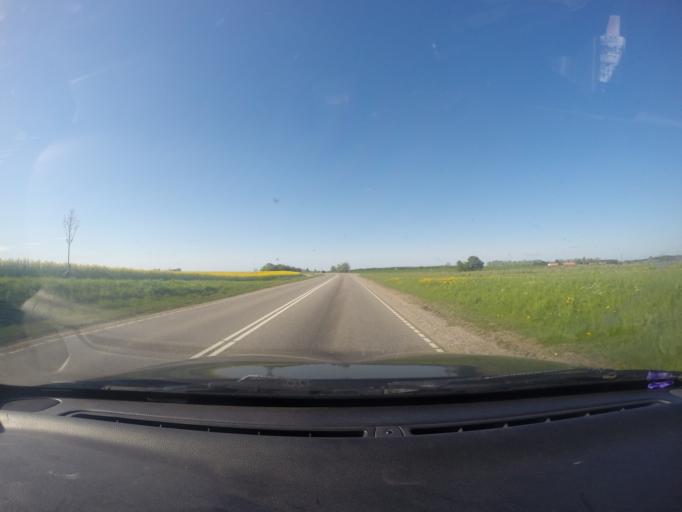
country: DK
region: Capital Region
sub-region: Hoje-Taastrup Kommune
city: Taastrup
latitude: 55.6704
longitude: 12.2740
